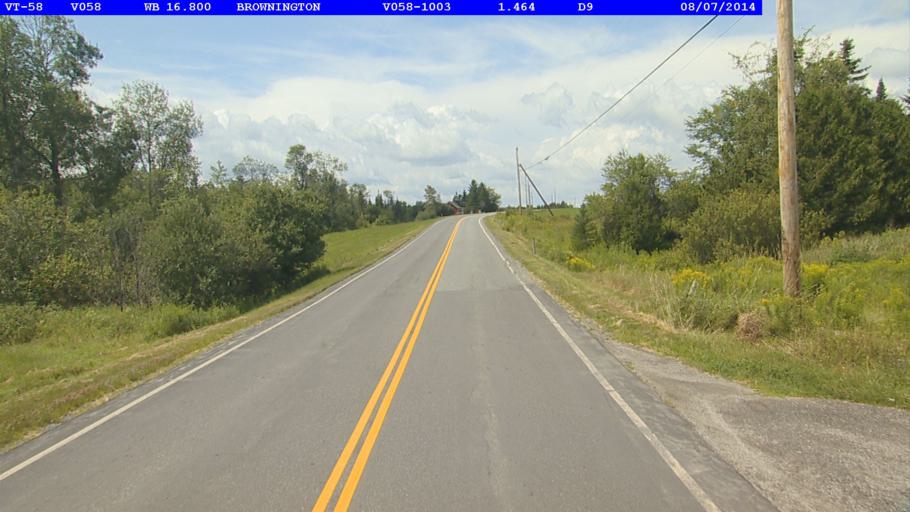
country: US
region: Vermont
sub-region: Orleans County
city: Newport
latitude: 44.7995
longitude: -72.1175
